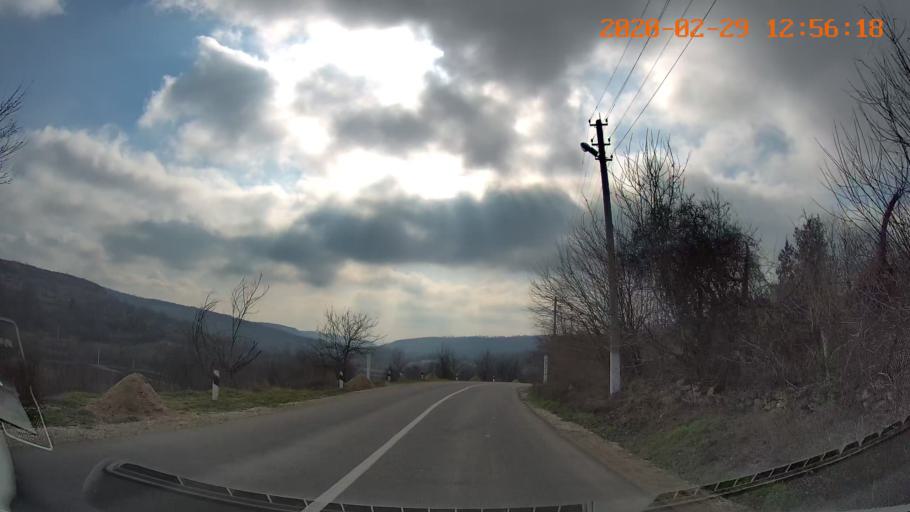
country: MD
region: Telenesti
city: Camenca
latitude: 48.0881
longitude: 28.7226
